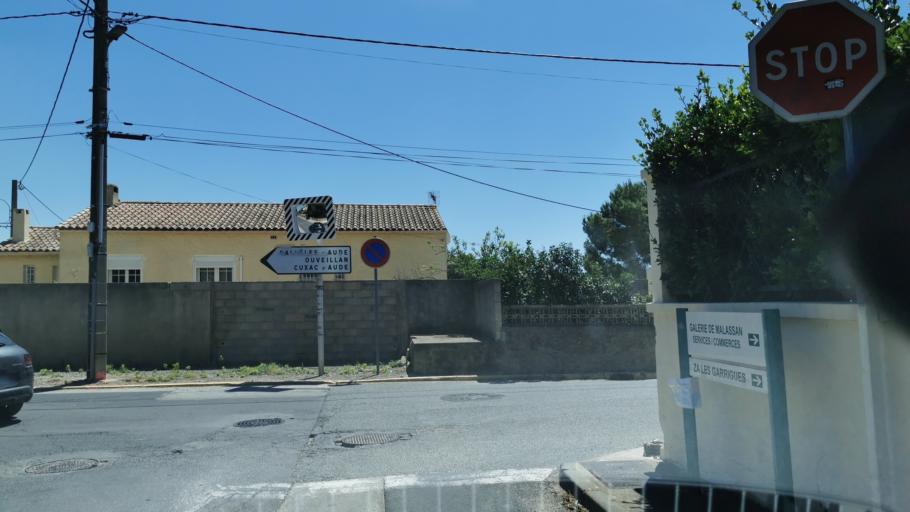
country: FR
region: Languedoc-Roussillon
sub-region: Departement de l'Aude
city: Saint-Marcel-sur-Aude
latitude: 43.2455
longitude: 2.9250
